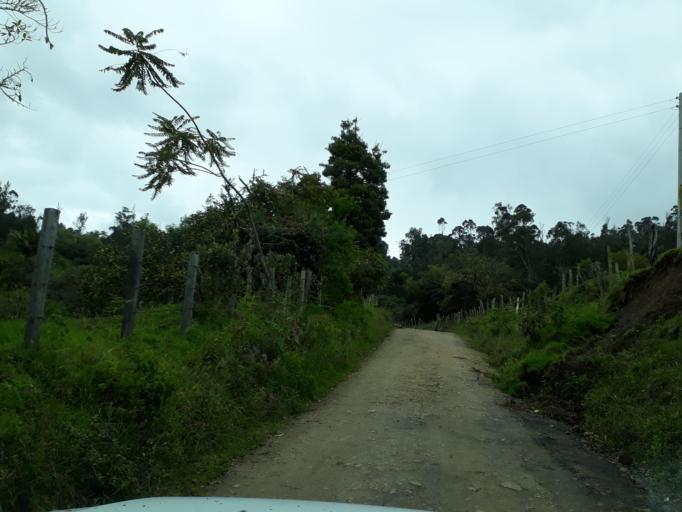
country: CO
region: Cundinamarca
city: Junin
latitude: 4.7873
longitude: -73.6553
